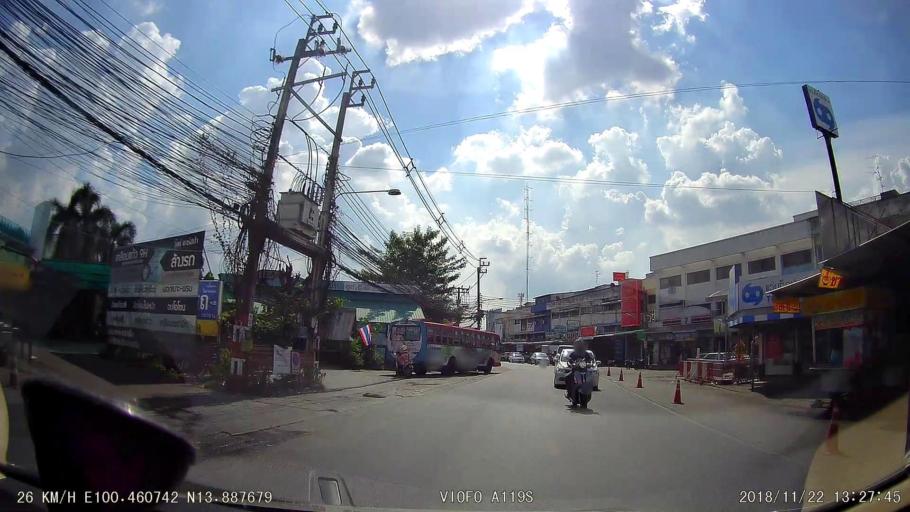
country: TH
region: Nonthaburi
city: Bang Bua Thong
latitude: 13.8876
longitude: 100.4607
